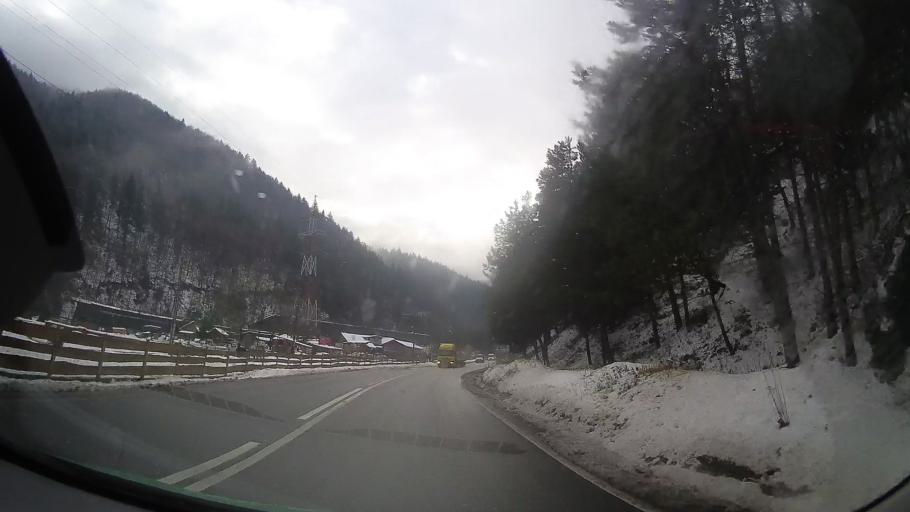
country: RO
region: Neamt
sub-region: Comuna Bicaz
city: Bicaz
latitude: 46.8969
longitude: 26.0529
